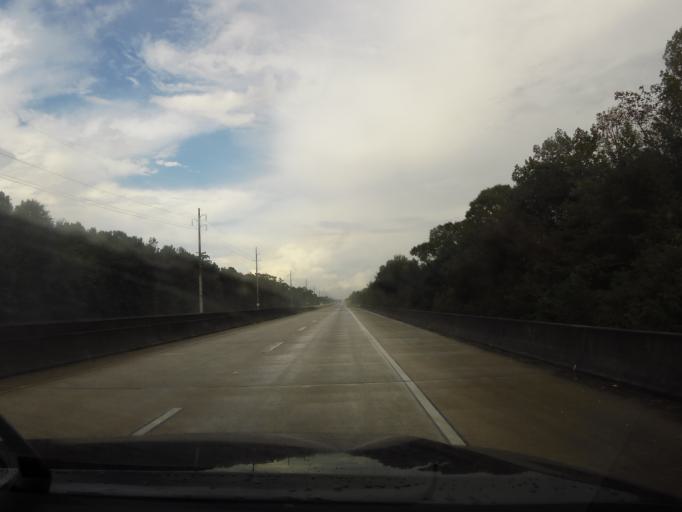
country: US
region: Georgia
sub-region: Long County
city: Ludowici
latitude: 31.6860
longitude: -81.7964
